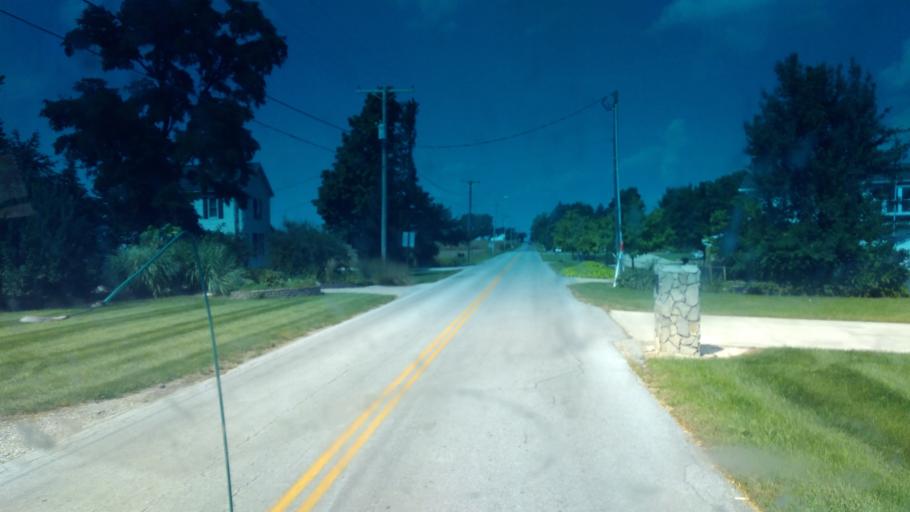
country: US
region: Ohio
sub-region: Hardin County
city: Ada
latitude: 40.7112
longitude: -83.9229
